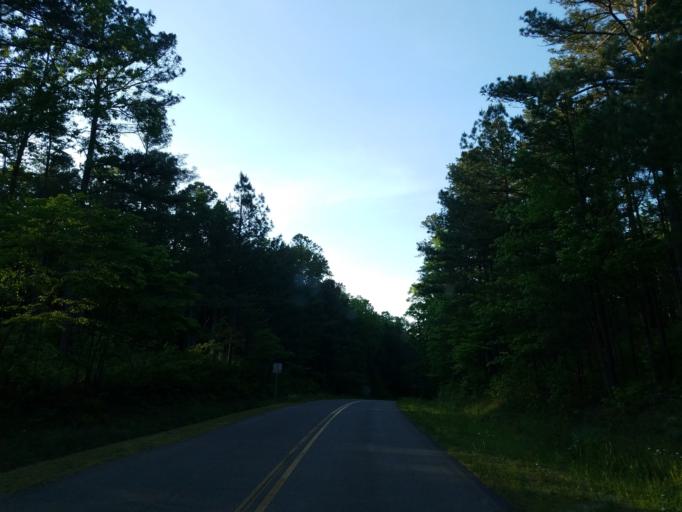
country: US
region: Georgia
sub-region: Whitfield County
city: Dalton
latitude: 34.6277
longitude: -85.0803
